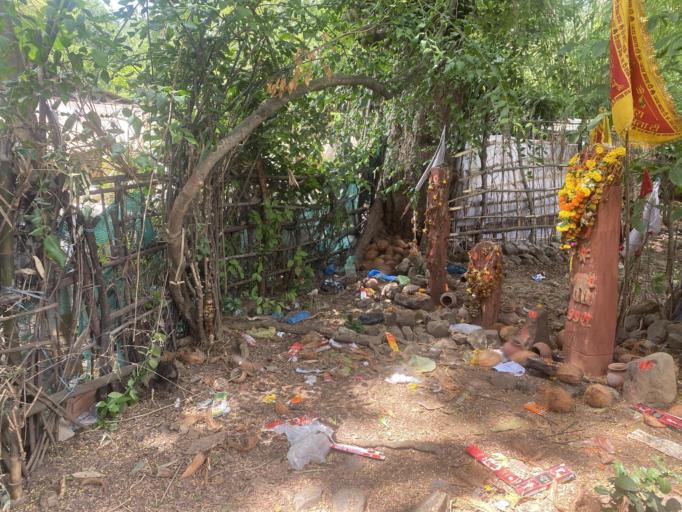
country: IN
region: Gujarat
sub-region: Valsad
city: Vapi
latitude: 20.3182
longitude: 72.8357
